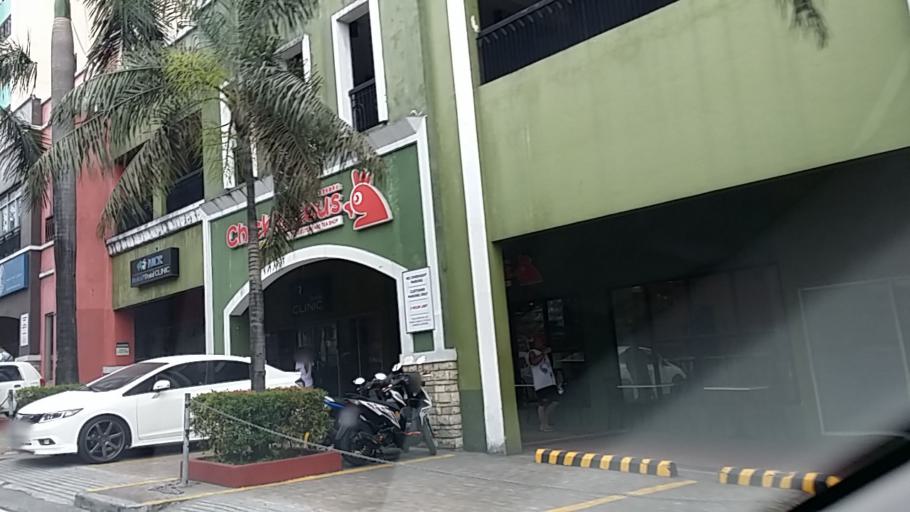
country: PH
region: Metro Manila
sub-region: Mandaluyong
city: Mandaluyong City
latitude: 14.5794
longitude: 121.0468
